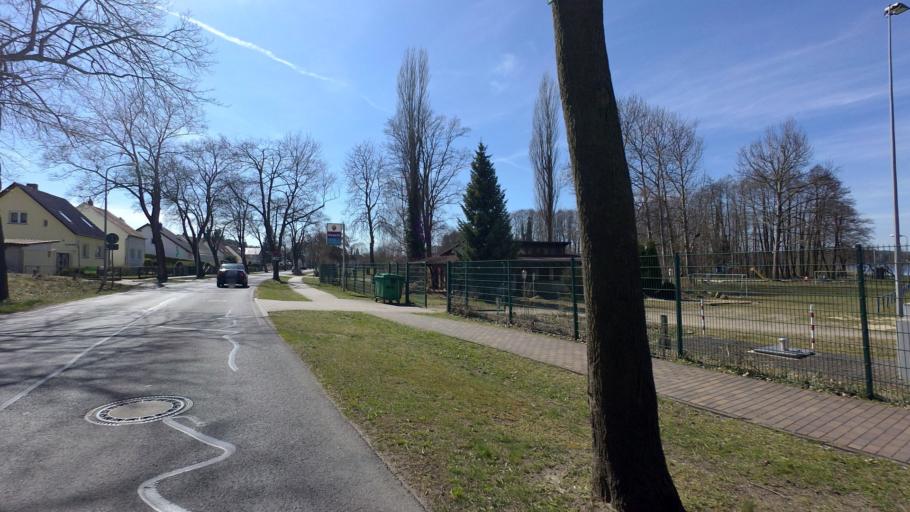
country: DE
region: Brandenburg
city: Mittenwalde
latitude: 52.2126
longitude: 13.5855
